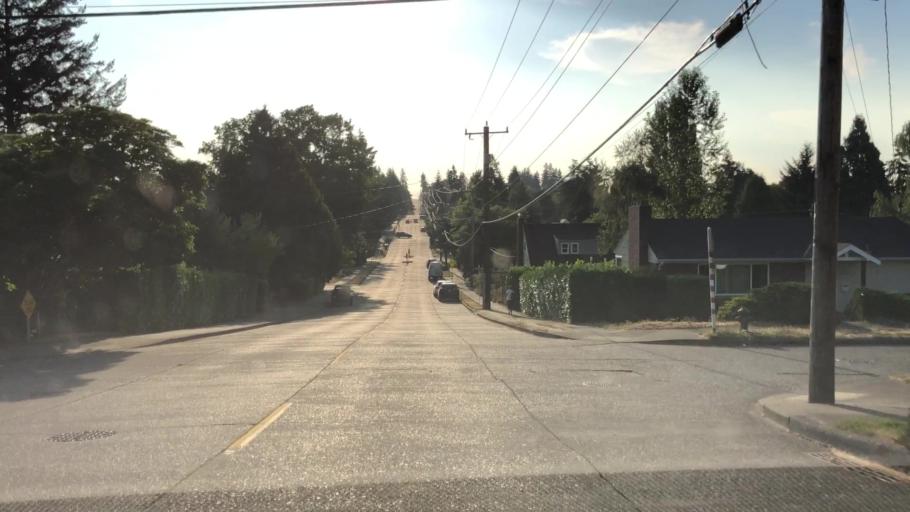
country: US
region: Washington
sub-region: King County
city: Inglewood-Finn Hill
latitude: 47.6794
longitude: -122.2885
